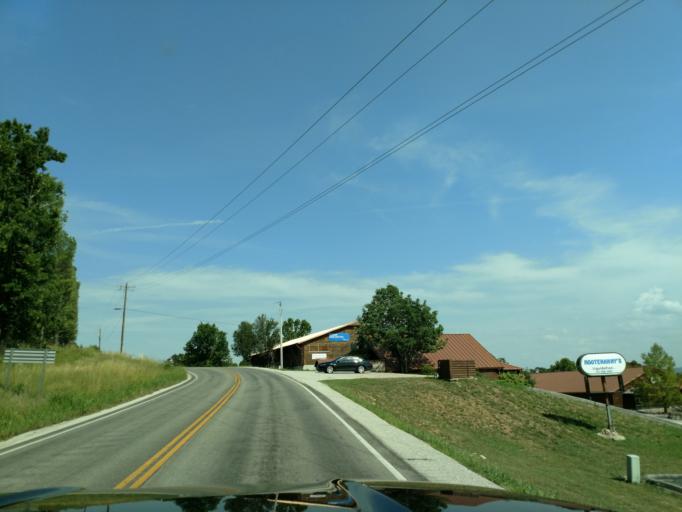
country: US
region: Missouri
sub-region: Barry County
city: Shell Knob
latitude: 36.6215
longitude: -93.6158
